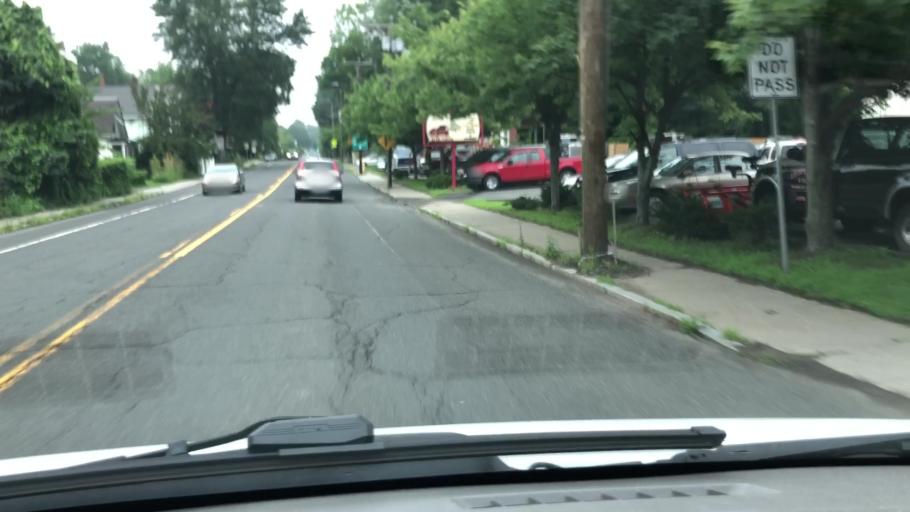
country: US
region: Massachusetts
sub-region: Franklin County
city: Greenfield
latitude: 42.5766
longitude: -72.5977
